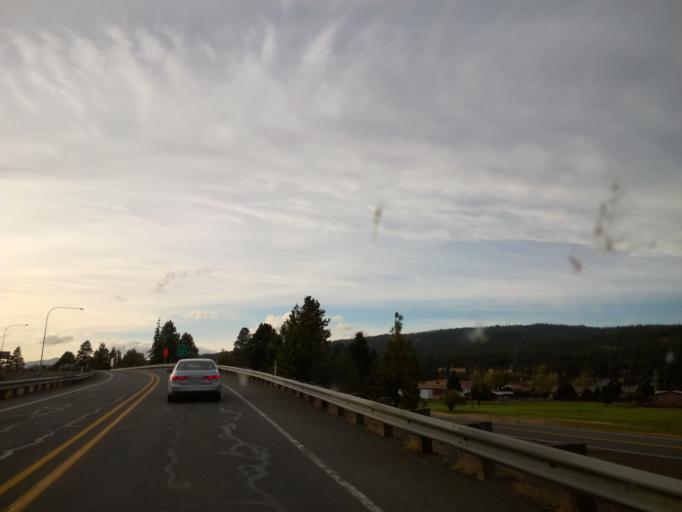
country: US
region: Washington
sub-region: Kittitas County
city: Cle Elum
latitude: 47.1873
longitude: -120.8987
